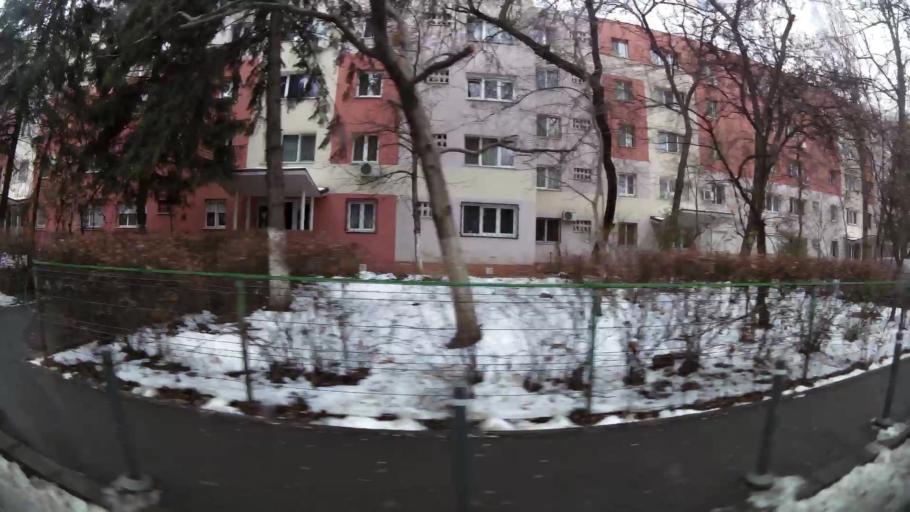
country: RO
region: Ilfov
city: Dobroesti
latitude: 44.4243
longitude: 26.1657
